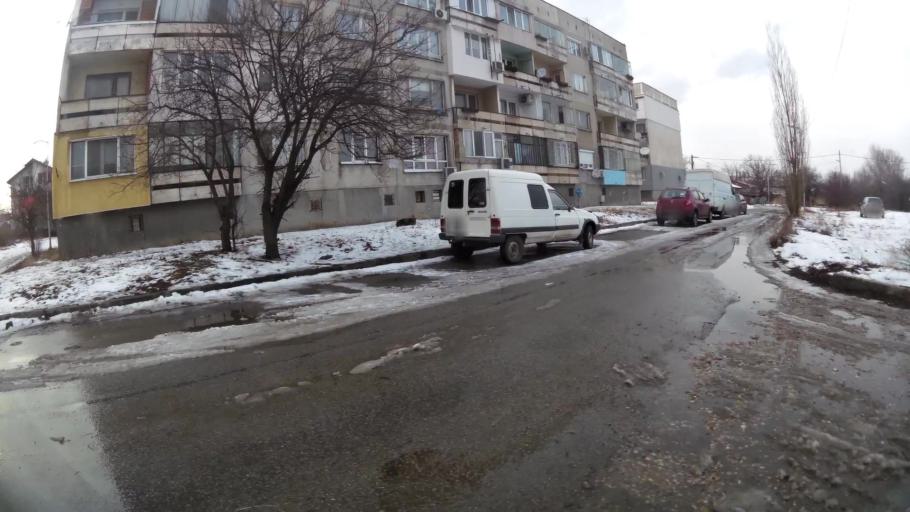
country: BG
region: Sofia-Capital
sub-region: Stolichna Obshtina
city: Sofia
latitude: 42.7280
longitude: 23.3455
